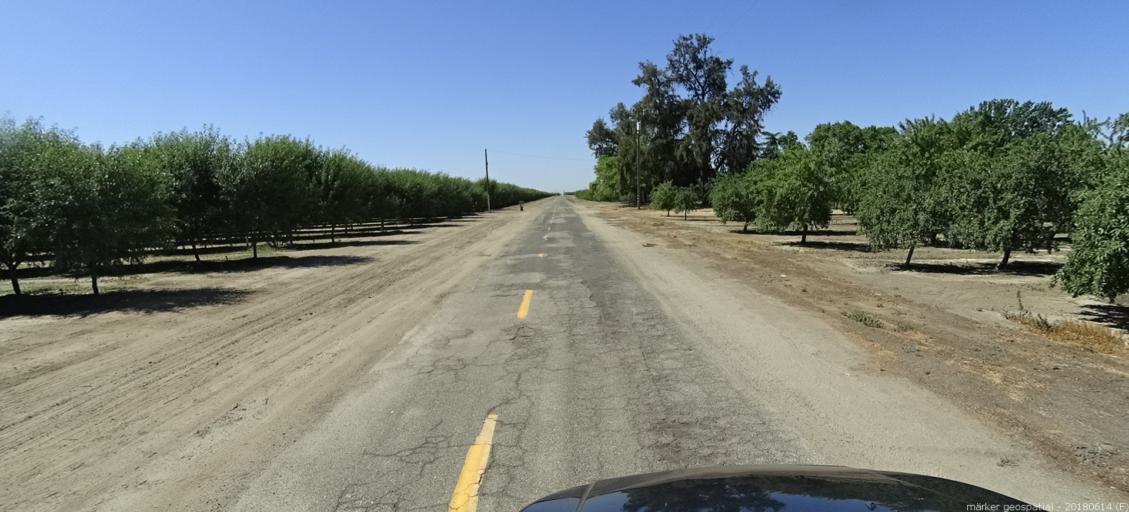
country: US
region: California
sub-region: Madera County
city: Fairmead
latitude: 36.9629
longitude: -120.2203
